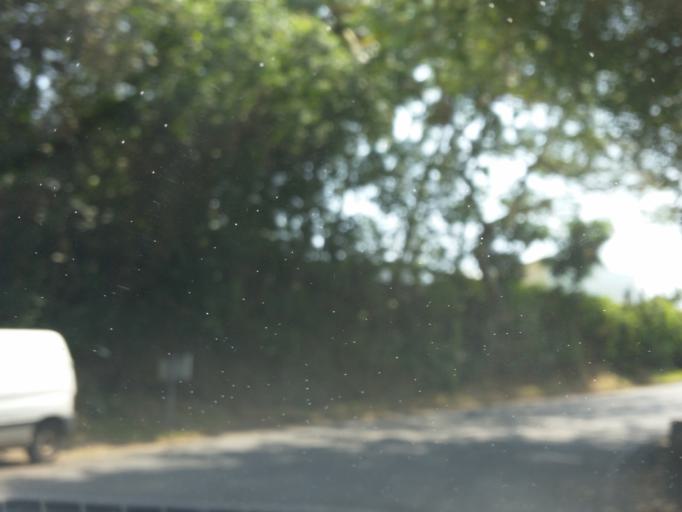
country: RE
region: Reunion
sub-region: Reunion
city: Sainte-Marie
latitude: -20.9091
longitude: 55.5040
